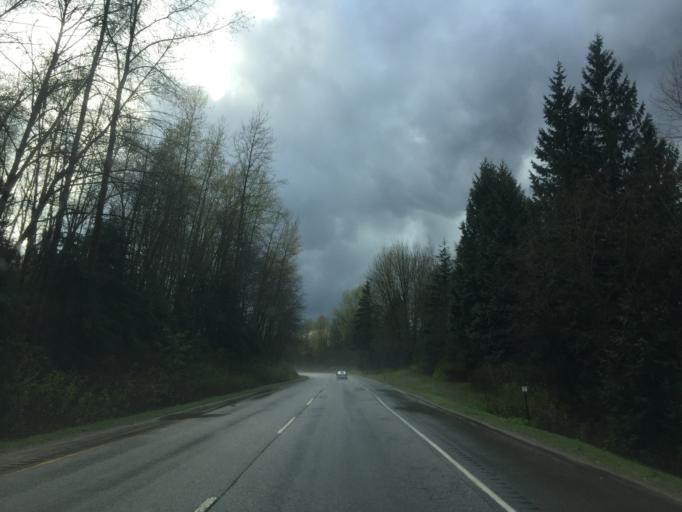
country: CA
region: British Columbia
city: Agassiz
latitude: 49.2156
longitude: -121.6967
